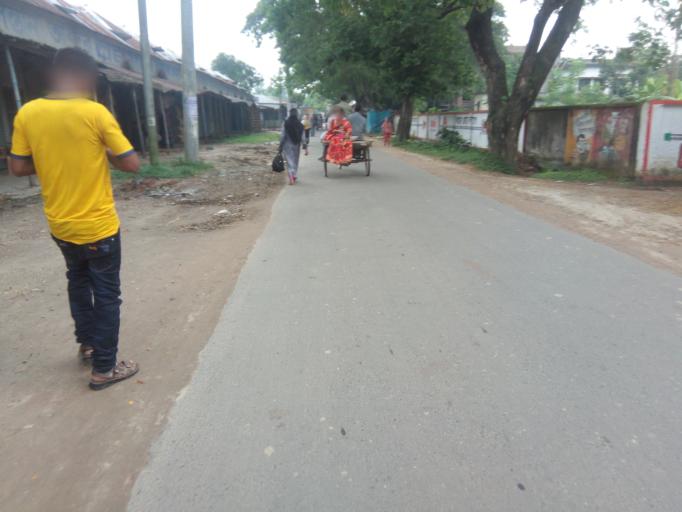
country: BD
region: Dhaka
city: Faridpur
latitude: 23.5449
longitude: 89.6302
